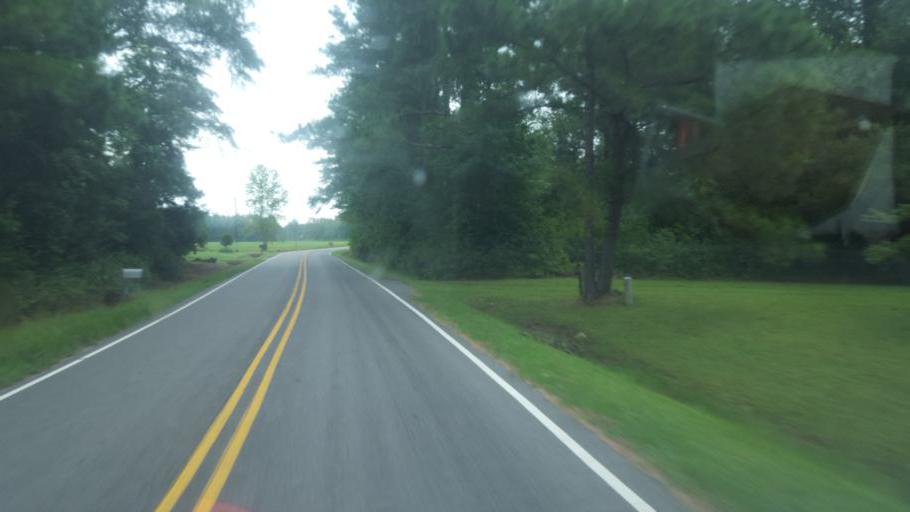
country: US
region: North Carolina
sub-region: Tyrrell County
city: Columbia
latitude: 35.9448
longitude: -76.2982
